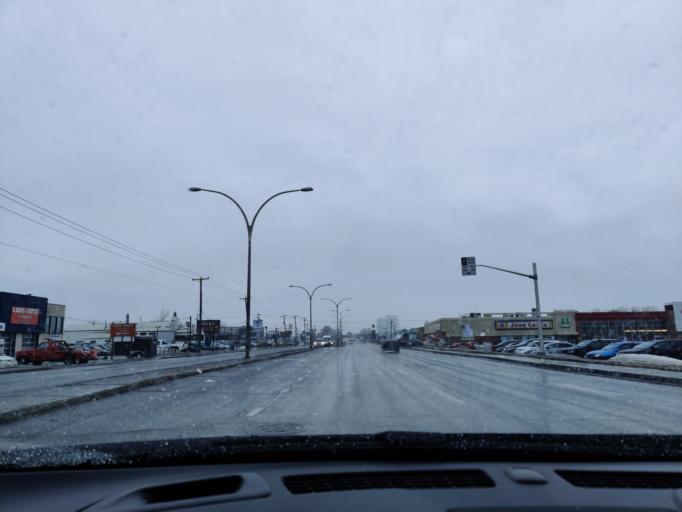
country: CA
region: Quebec
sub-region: Laval
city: Laval
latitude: 45.5578
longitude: -73.7676
